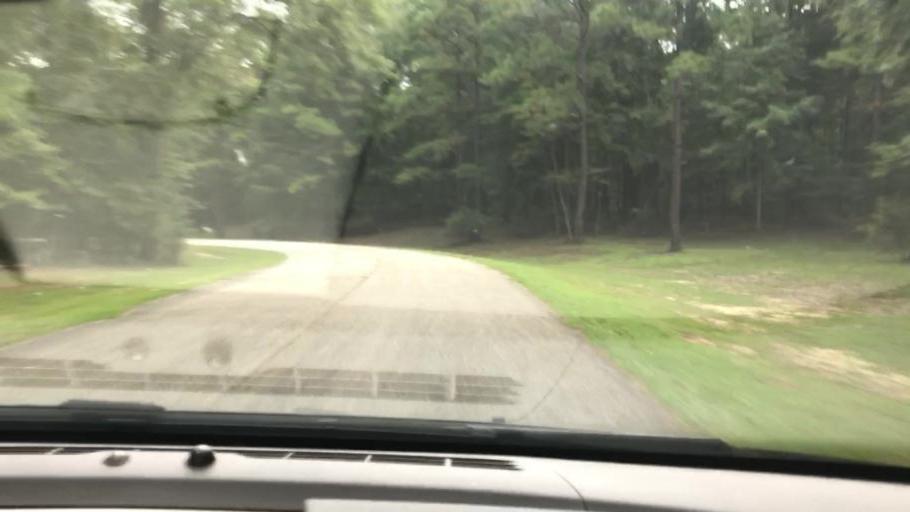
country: US
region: Georgia
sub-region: Clay County
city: Fort Gaines
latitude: 31.6668
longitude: -85.0514
